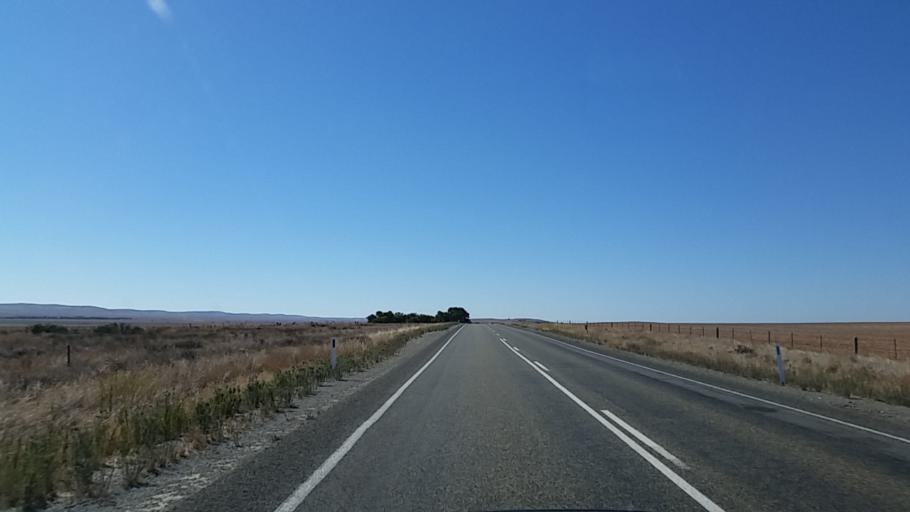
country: AU
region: South Australia
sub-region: Northern Areas
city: Jamestown
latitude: -33.2618
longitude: 138.8698
